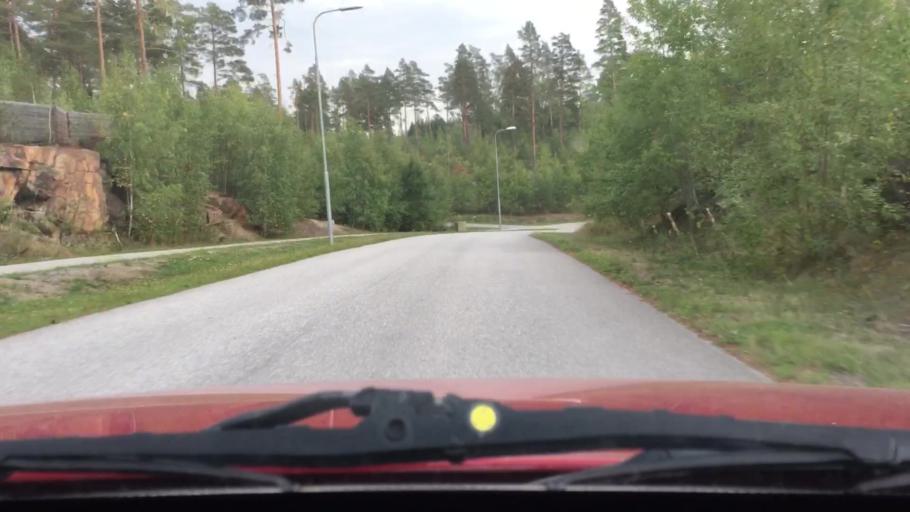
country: FI
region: Varsinais-Suomi
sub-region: Turku
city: Masku
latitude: 60.5591
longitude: 22.1401
